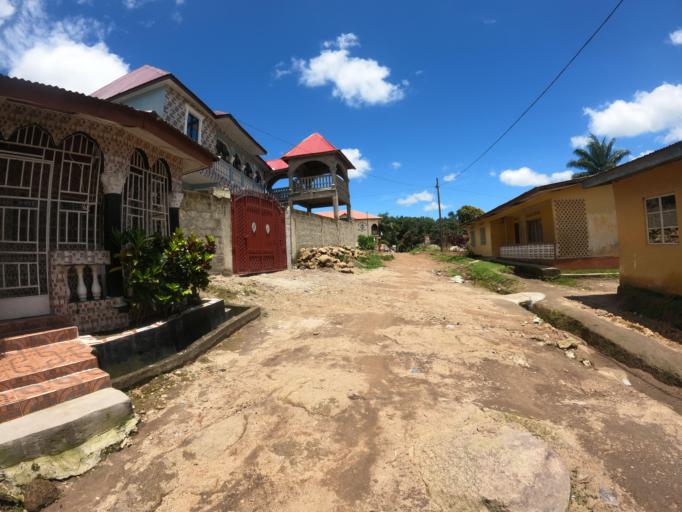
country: SL
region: Northern Province
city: Makeni
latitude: 8.8961
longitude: -12.0606
